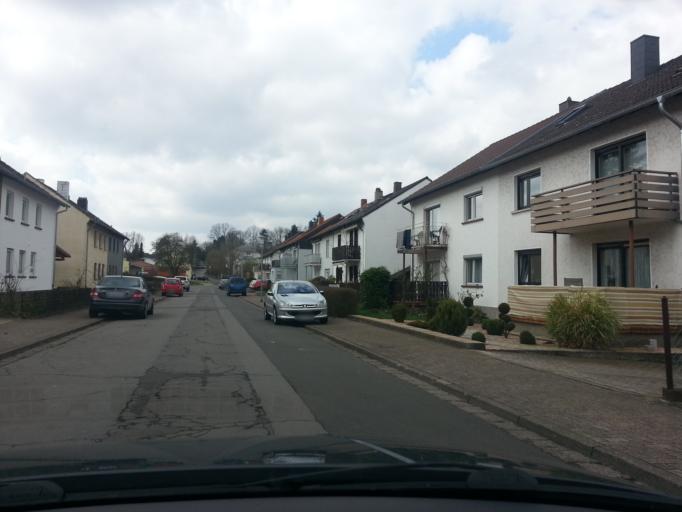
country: DE
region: Saarland
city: Neunkirchen
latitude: 49.3264
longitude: 7.2181
